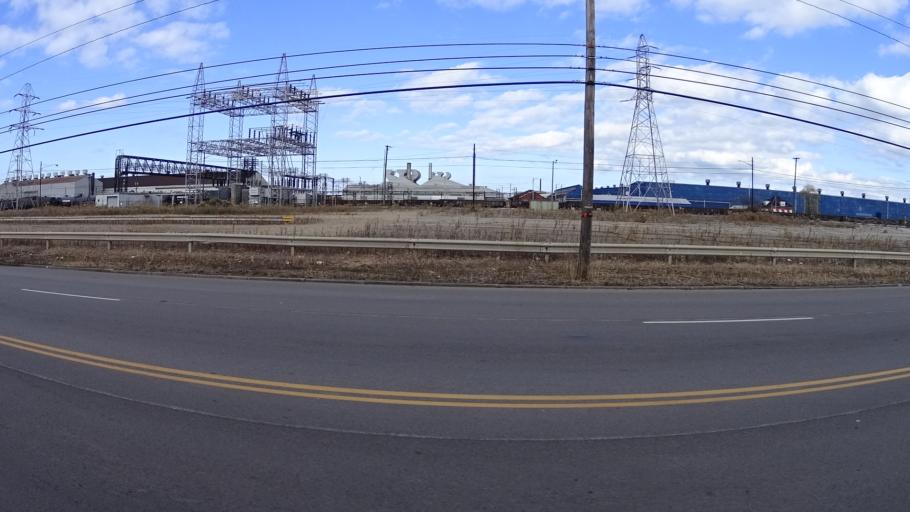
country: US
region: Ohio
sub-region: Lorain County
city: Sheffield
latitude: 41.4456
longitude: -82.1256
